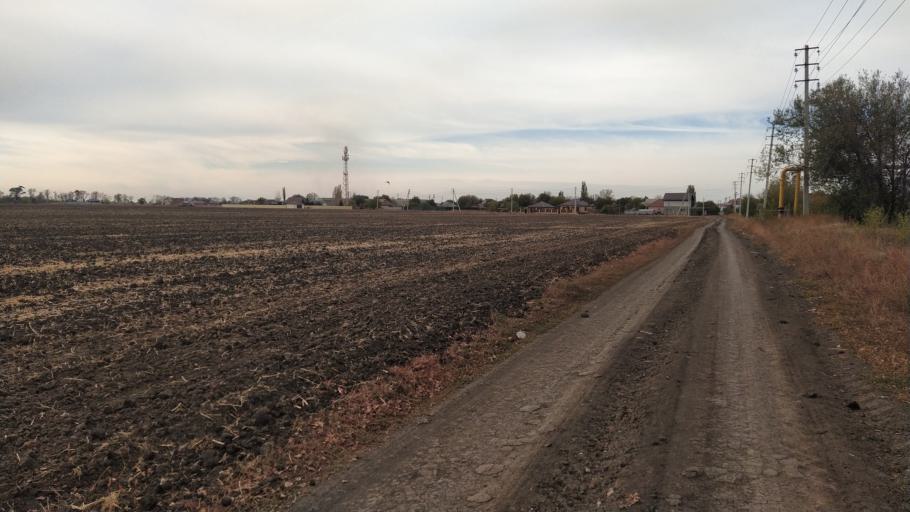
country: RU
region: Rostov
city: Bataysk
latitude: 47.1110
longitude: 39.6814
